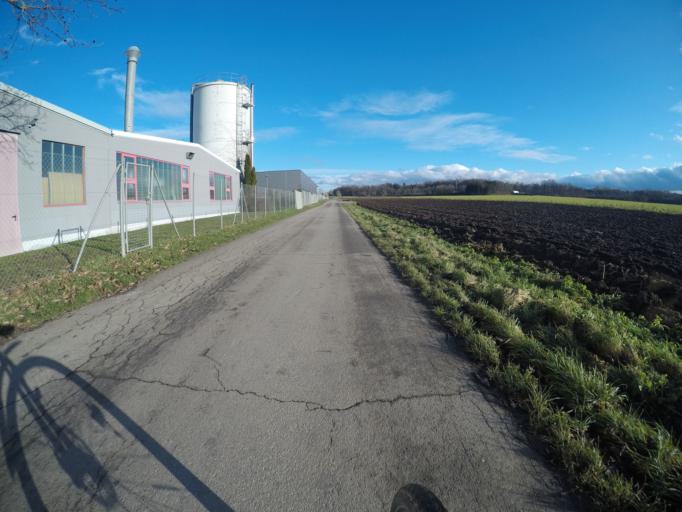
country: DE
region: Baden-Wuerttemberg
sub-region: Regierungsbezirk Stuttgart
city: Bondorf
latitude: 48.5272
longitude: 8.8786
